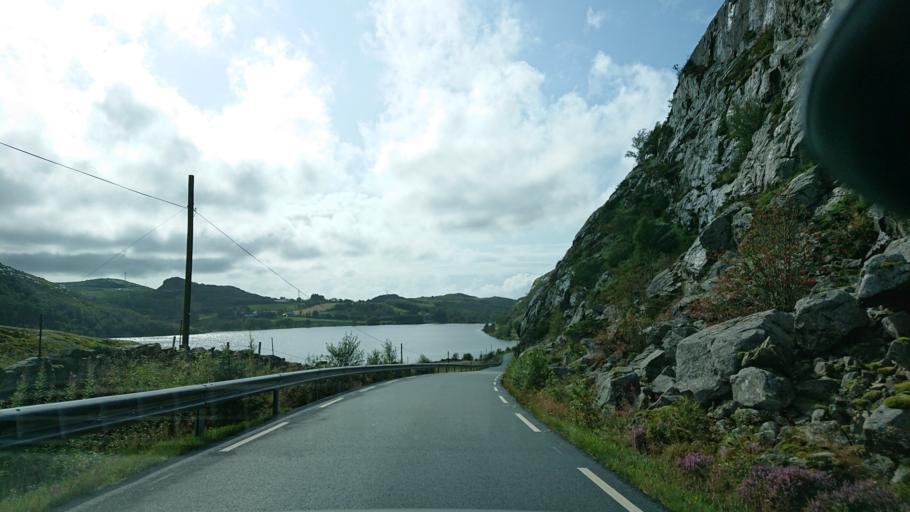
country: NO
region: Rogaland
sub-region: Gjesdal
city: Algard
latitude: 58.6775
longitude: 5.8436
